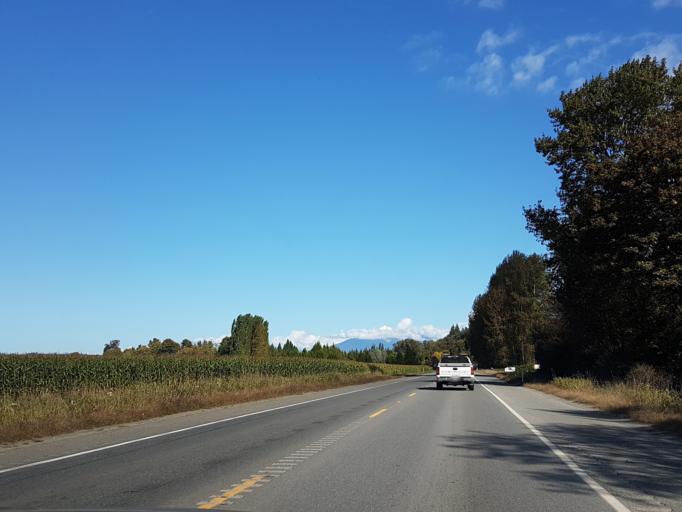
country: US
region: Washington
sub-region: Snohomish County
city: Monroe
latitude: 47.8204
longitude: -121.9762
